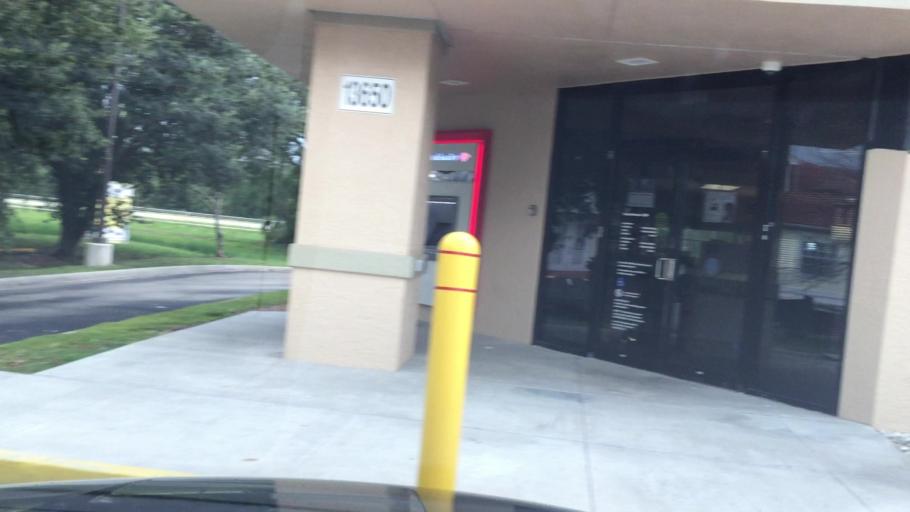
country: US
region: Florida
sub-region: Lee County
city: Villas
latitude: 26.5450
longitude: -81.8404
